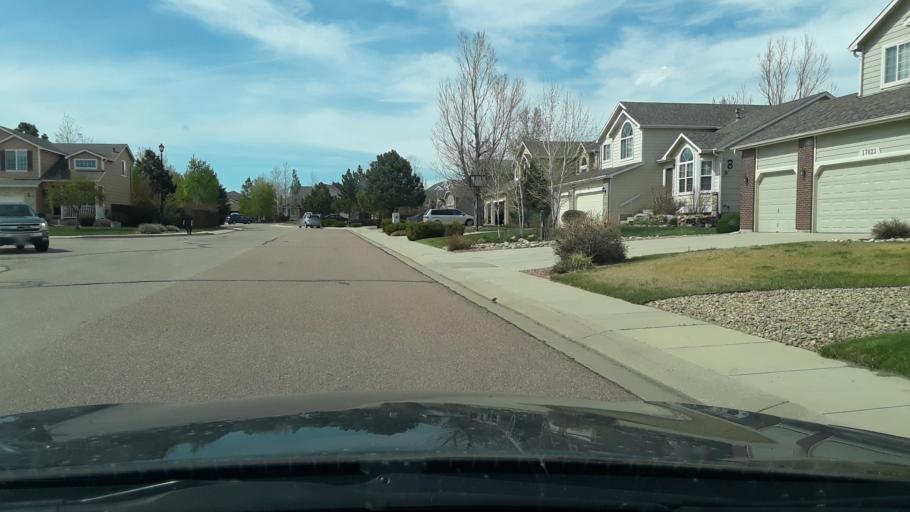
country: US
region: Colorado
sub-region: El Paso County
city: Monument
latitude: 39.0772
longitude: -104.8642
